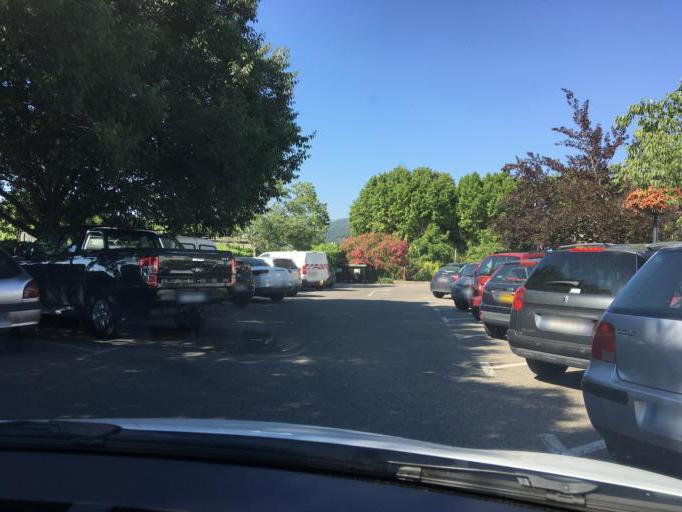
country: FR
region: Provence-Alpes-Cote d'Azur
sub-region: Departement des Alpes-de-Haute-Provence
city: Peyruis
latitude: 44.0263
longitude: 5.9390
